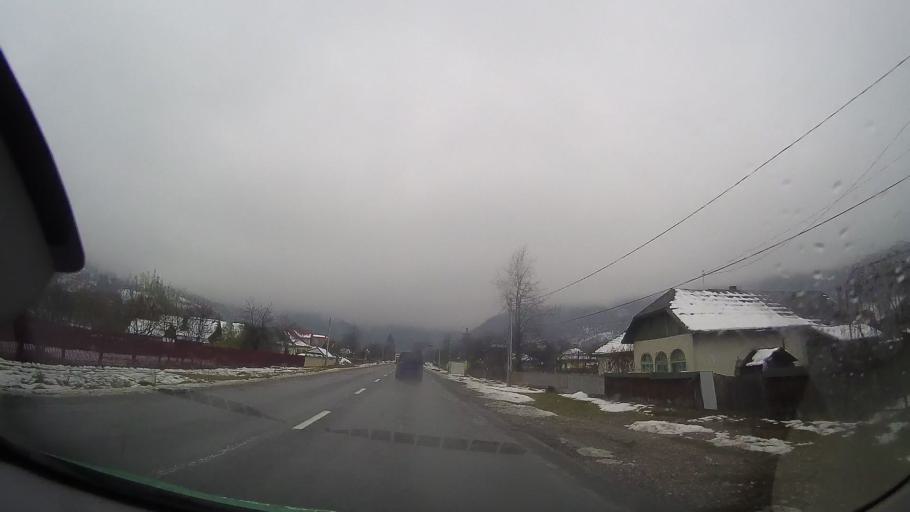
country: RO
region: Neamt
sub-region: Comuna Pangarati
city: Stejaru
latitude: 46.9061
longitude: 26.1764
